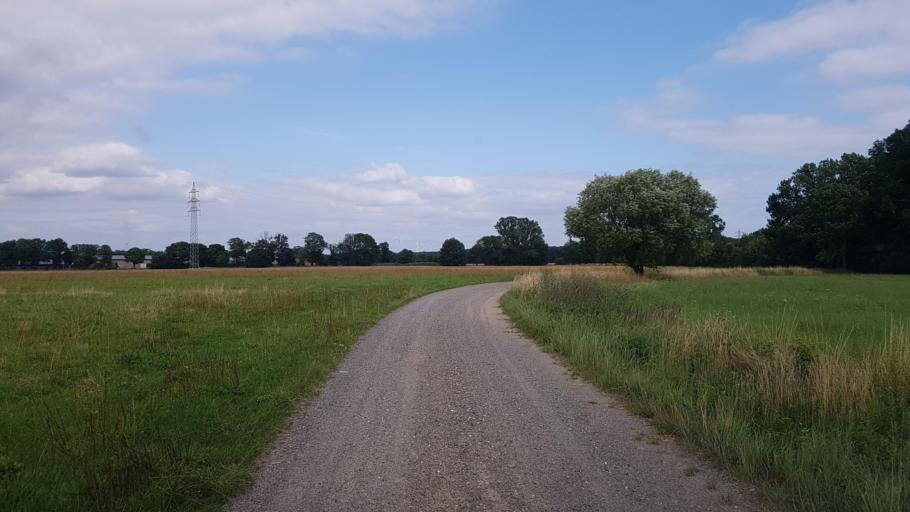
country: DE
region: Brandenburg
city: Bronkow
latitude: 51.6132
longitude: 13.9008
